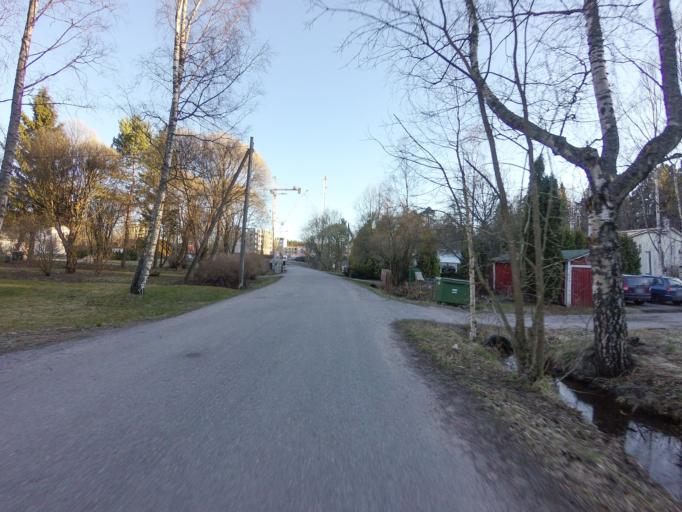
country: FI
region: Uusimaa
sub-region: Helsinki
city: Helsinki
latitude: 60.1718
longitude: 25.0196
